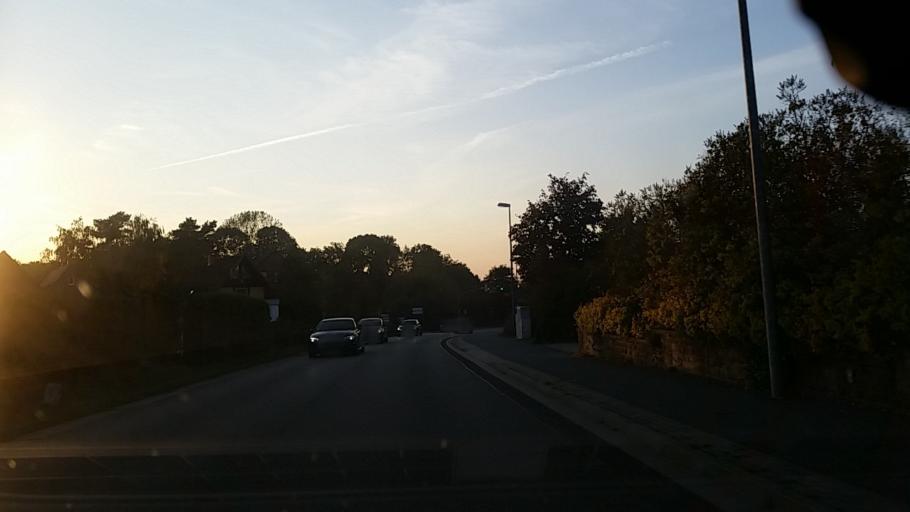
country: DE
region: Lower Saxony
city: Wolfsburg
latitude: 52.4197
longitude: 10.8426
